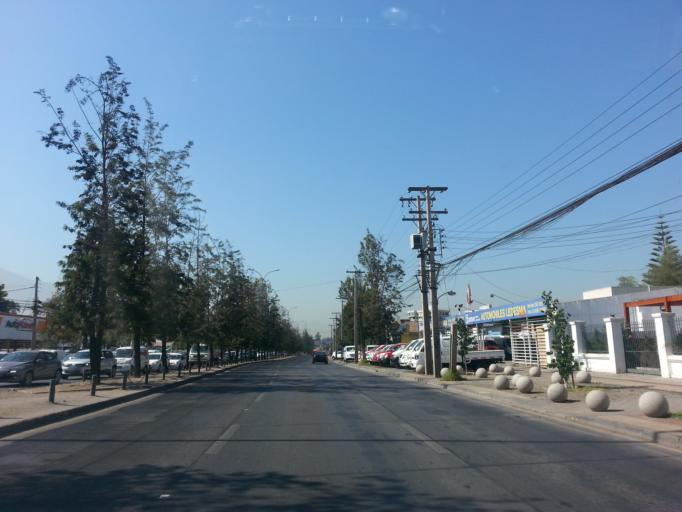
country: CL
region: Santiago Metropolitan
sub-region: Provincia de Santiago
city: Villa Presidente Frei, Nunoa, Santiago, Chile
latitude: -33.4323
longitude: -70.5748
